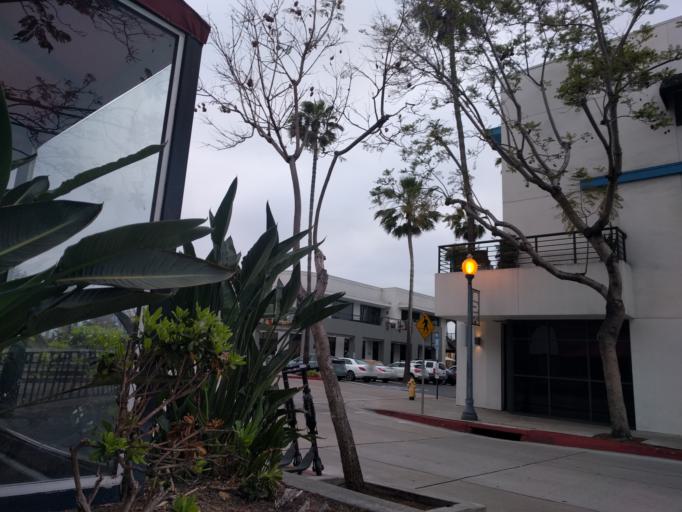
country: US
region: California
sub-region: San Diego County
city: San Diego
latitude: 32.7499
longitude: -117.1535
